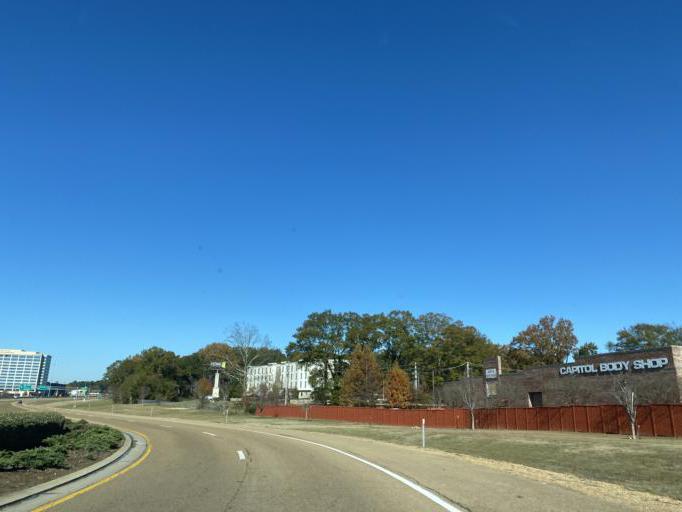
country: US
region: Mississippi
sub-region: Madison County
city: Ridgeland
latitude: 32.4309
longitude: -90.1425
